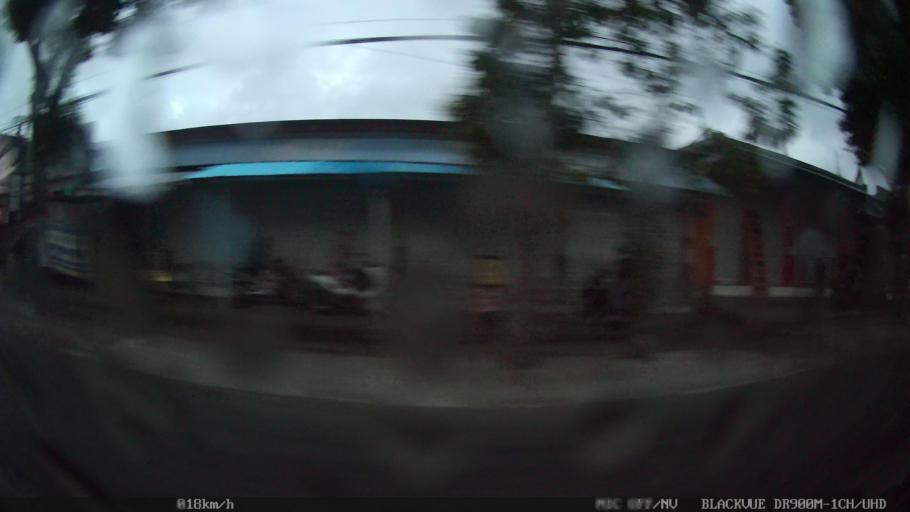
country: ID
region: Bali
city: Banjar Parekan
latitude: -8.5797
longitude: 115.2168
